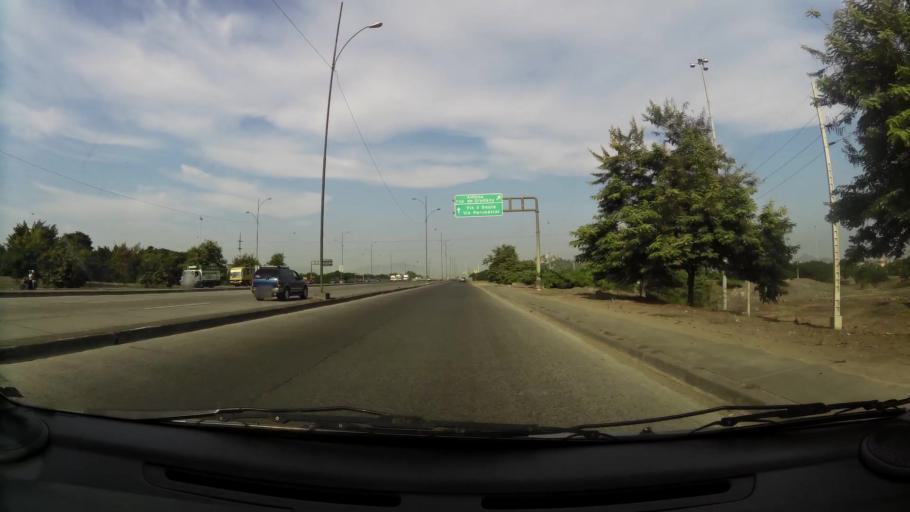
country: EC
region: Guayas
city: Eloy Alfaro
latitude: -2.0728
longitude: -79.9180
